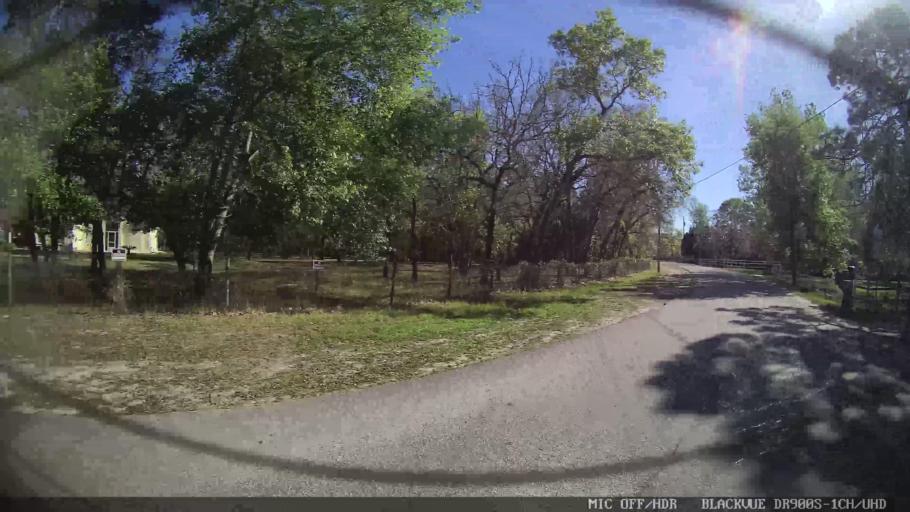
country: US
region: Florida
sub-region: Pasco County
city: Shady Hills
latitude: 28.4024
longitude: -82.5732
